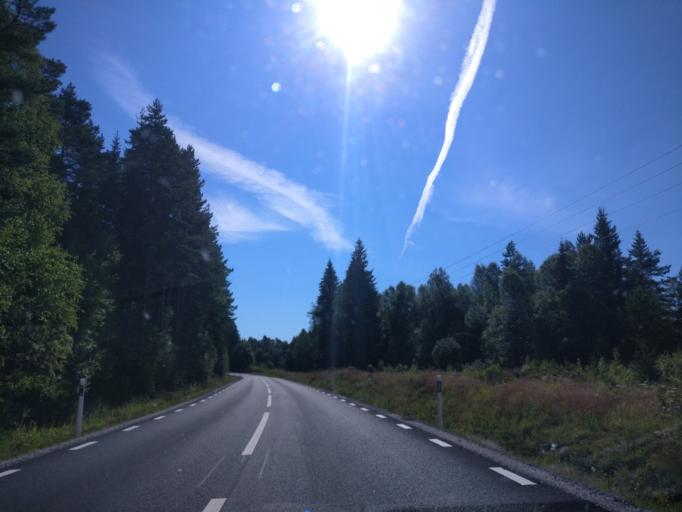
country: SE
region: Vaermland
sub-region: Hagfors Kommun
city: Hagfors
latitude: 60.0345
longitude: 13.8347
